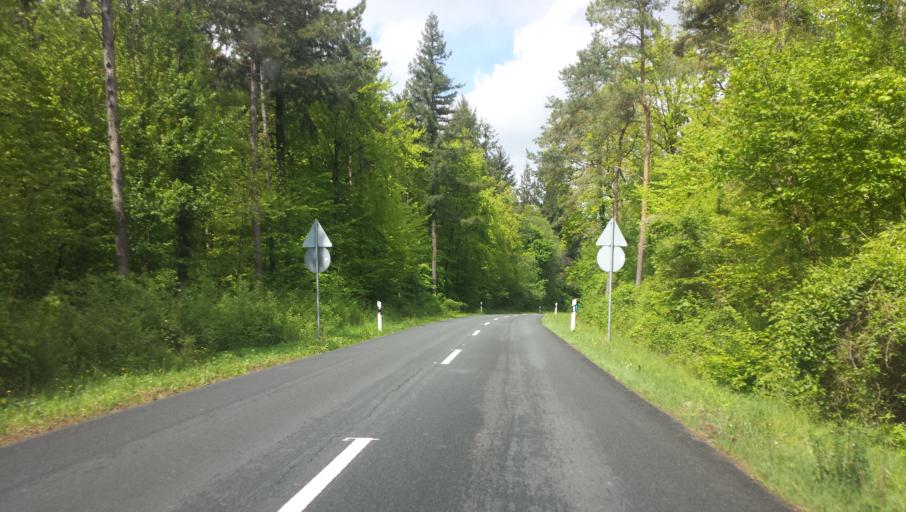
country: DE
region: Baden-Wuerttemberg
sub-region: Karlsruhe Region
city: Obrigheim
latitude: 49.3835
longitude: 9.1092
